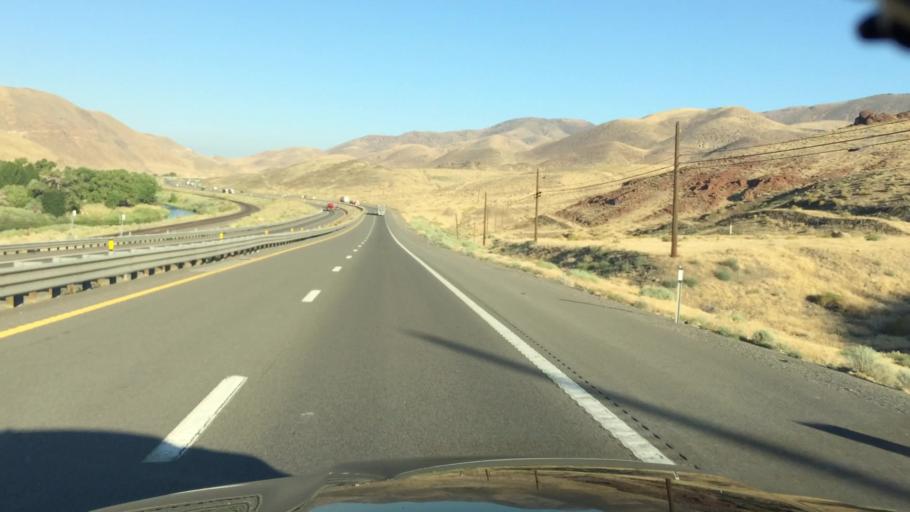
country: US
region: Nevada
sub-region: Lyon County
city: Fernley
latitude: 39.5912
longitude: -119.4074
